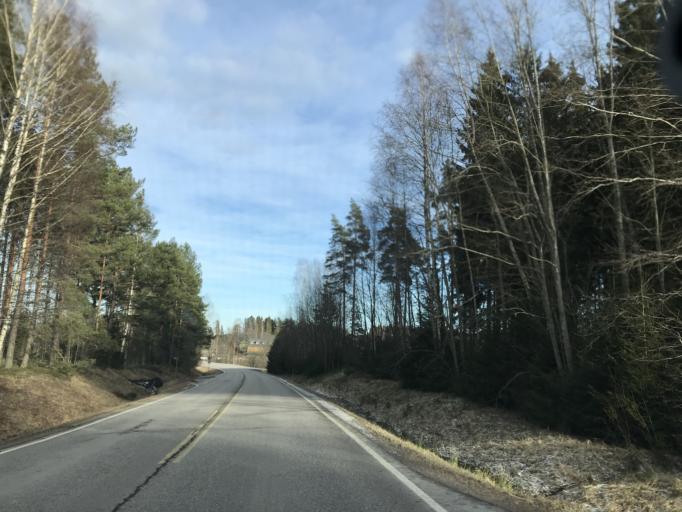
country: FI
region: Uusimaa
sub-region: Raaseporin
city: Ekenaes
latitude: 60.0824
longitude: 23.4014
